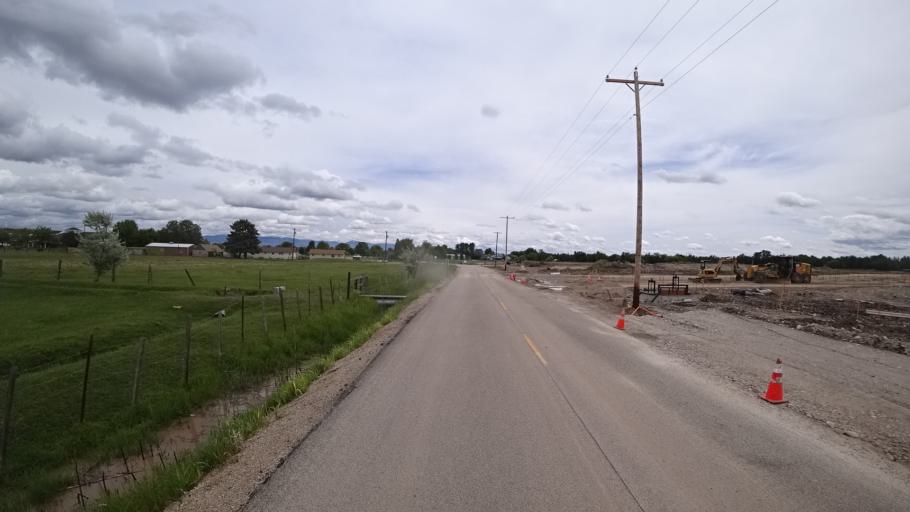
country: US
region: Idaho
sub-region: Ada County
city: Star
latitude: 43.6896
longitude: -116.4538
